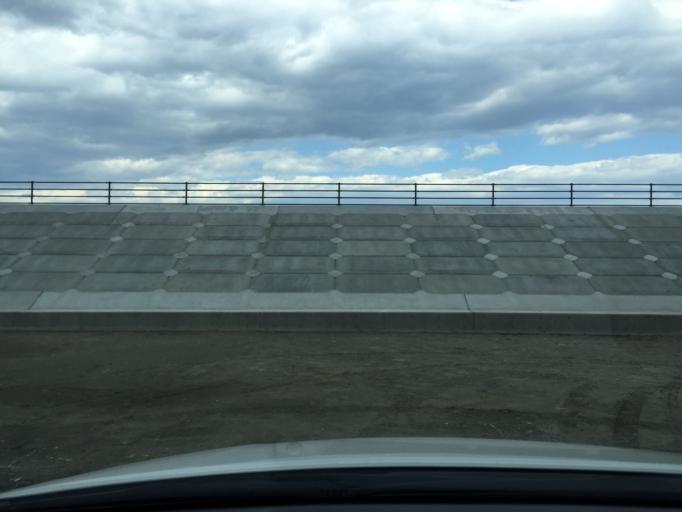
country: JP
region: Miyagi
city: Marumori
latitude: 37.7630
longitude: 140.9967
